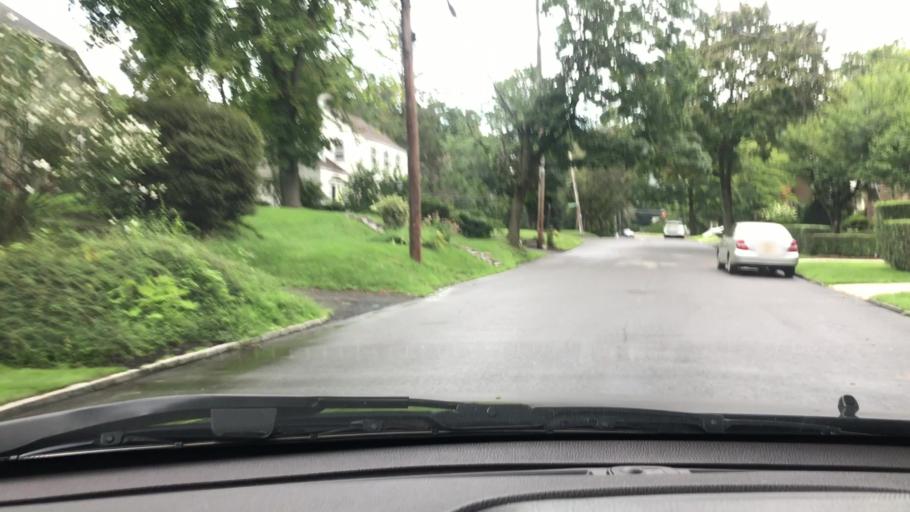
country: US
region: New York
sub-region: Westchester County
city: New Rochelle
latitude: 40.9341
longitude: -73.7928
